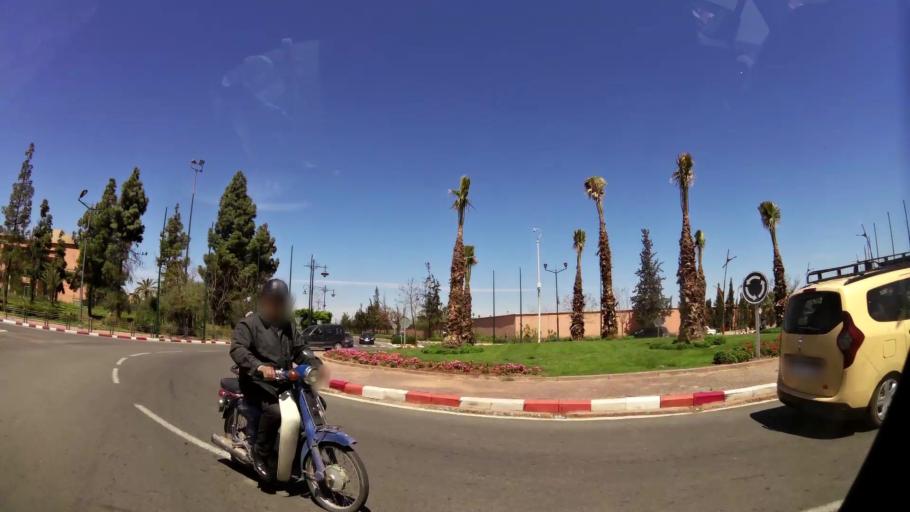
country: MA
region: Marrakech-Tensift-Al Haouz
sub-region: Marrakech
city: Marrakesh
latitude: 31.6133
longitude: -7.9930
